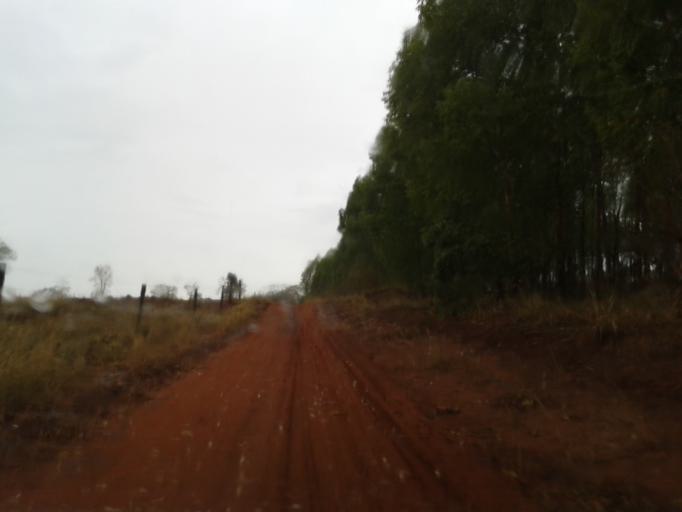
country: BR
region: Minas Gerais
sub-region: Campina Verde
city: Campina Verde
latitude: -19.3501
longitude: -49.5530
